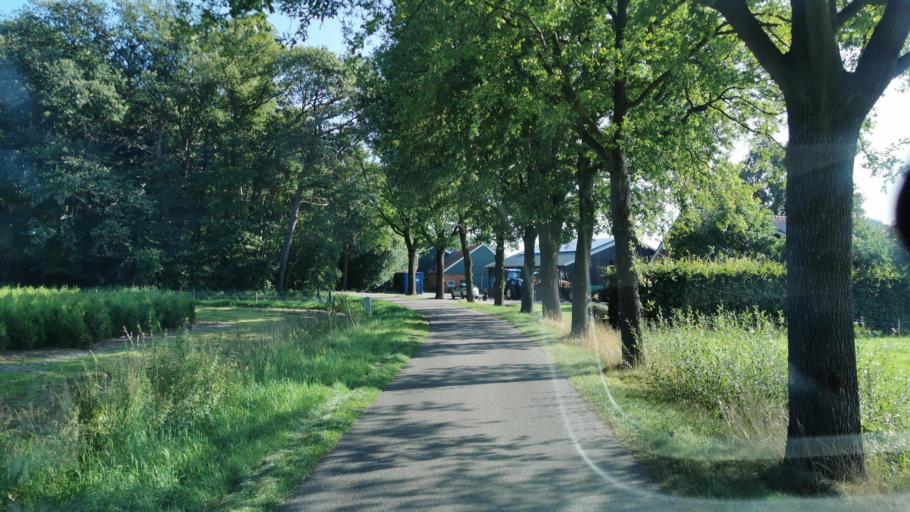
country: DE
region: Lower Saxony
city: Lage
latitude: 52.4197
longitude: 6.9468
